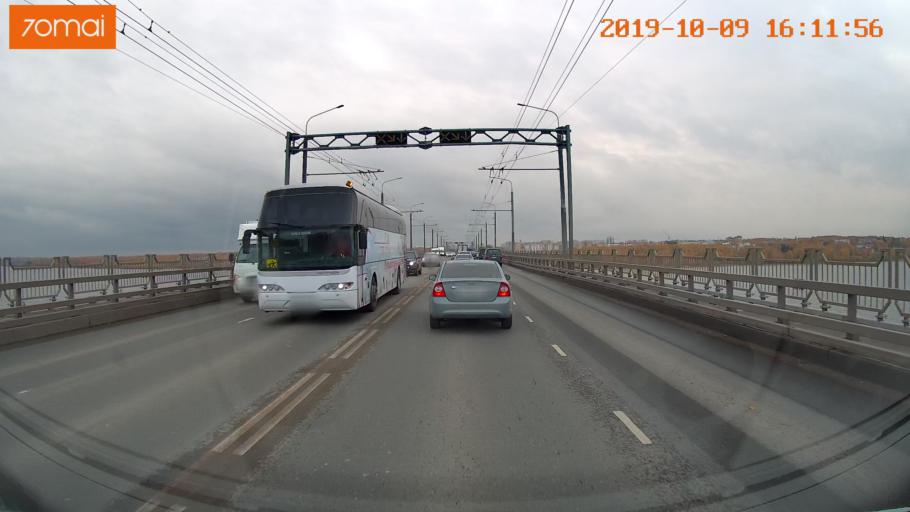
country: RU
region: Kostroma
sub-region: Kostromskoy Rayon
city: Kostroma
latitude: 57.7548
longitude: 40.9419
